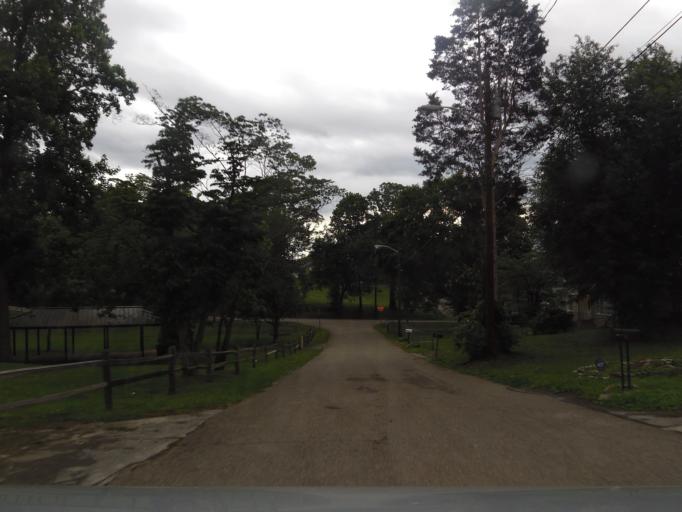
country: US
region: Tennessee
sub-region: Knox County
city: Knoxville
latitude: 35.9661
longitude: -83.9609
